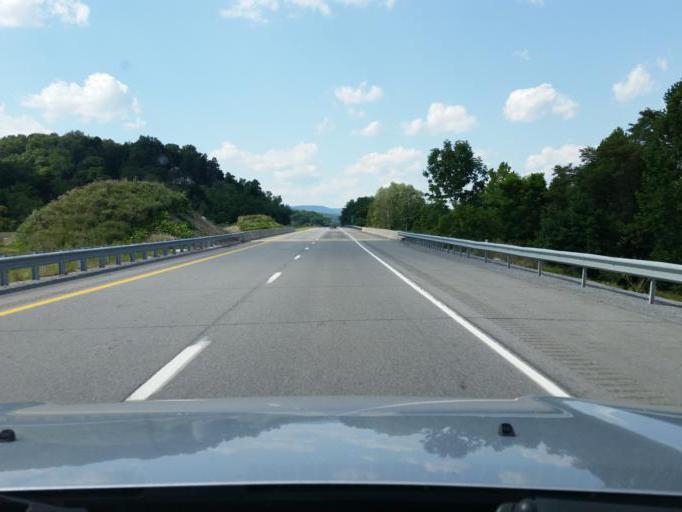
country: US
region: Pennsylvania
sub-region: Blair County
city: Duncansville
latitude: 40.4294
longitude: -78.4250
